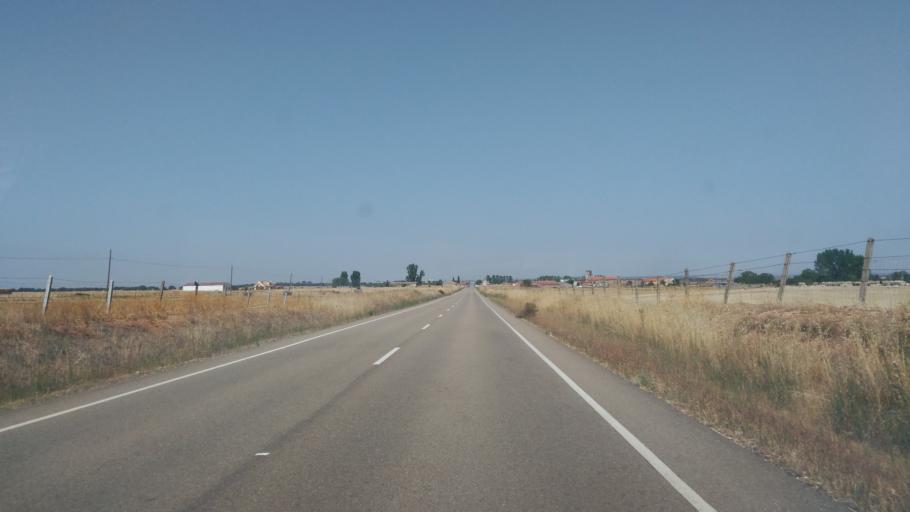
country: ES
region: Castille and Leon
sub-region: Provincia de Salamanca
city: La Fuente de San Esteban
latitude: 40.7714
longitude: -6.2242
